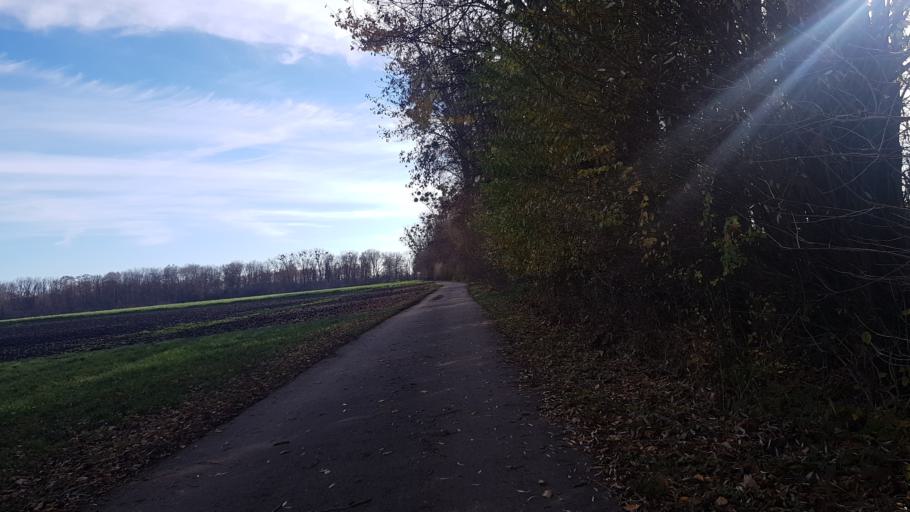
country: DE
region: Bavaria
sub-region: Upper Bavaria
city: Oberschleissheim
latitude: 48.2370
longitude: 11.5275
